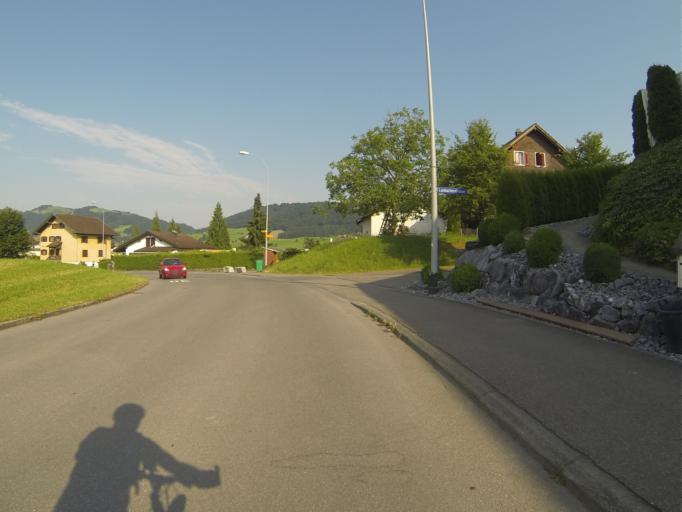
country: CH
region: Lucerne
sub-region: Lucerne-Land District
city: Buchrain
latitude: 47.0939
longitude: 8.3438
